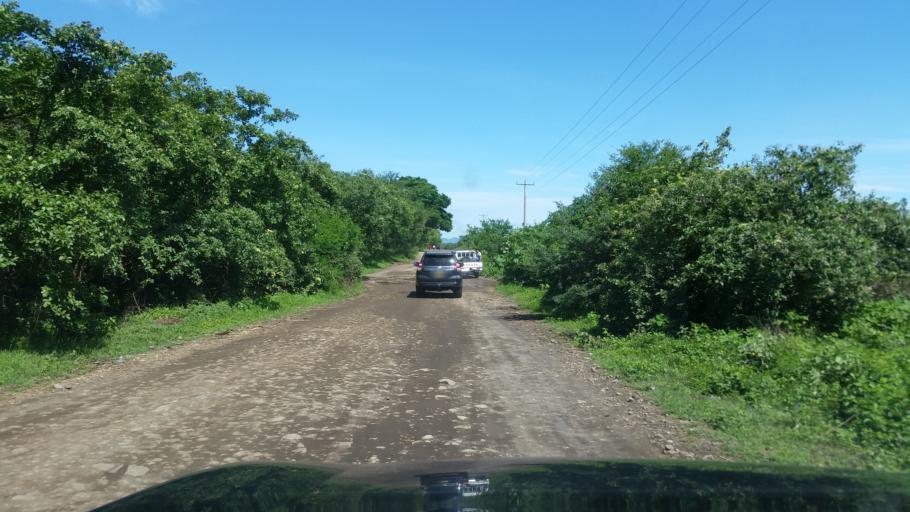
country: NI
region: Chinandega
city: Puerto Morazan
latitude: 12.7676
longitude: -87.0617
